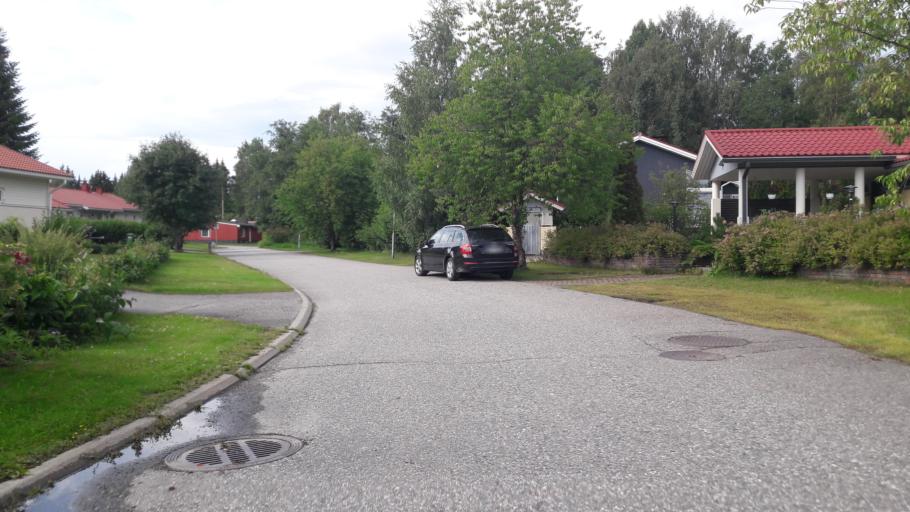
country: FI
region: North Karelia
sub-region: Joensuu
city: Joensuu
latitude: 62.5839
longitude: 29.8072
